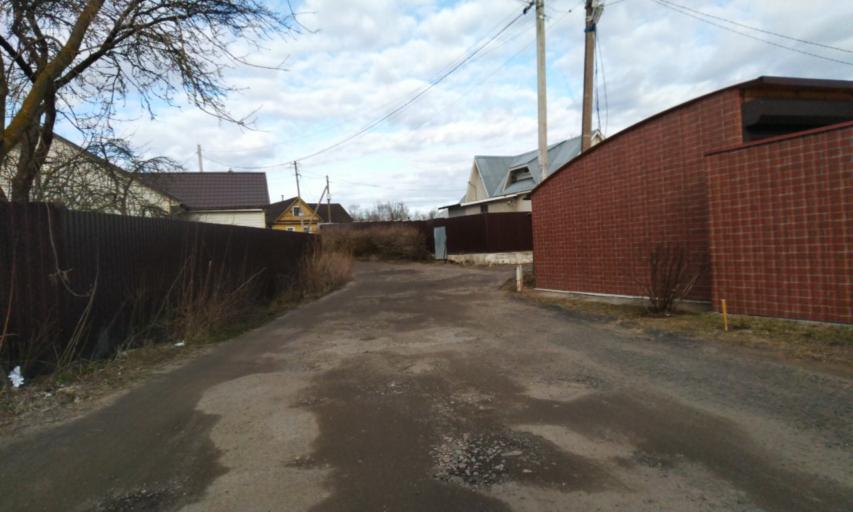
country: RU
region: Leningrad
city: Toksovo
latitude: 60.1233
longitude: 30.4869
